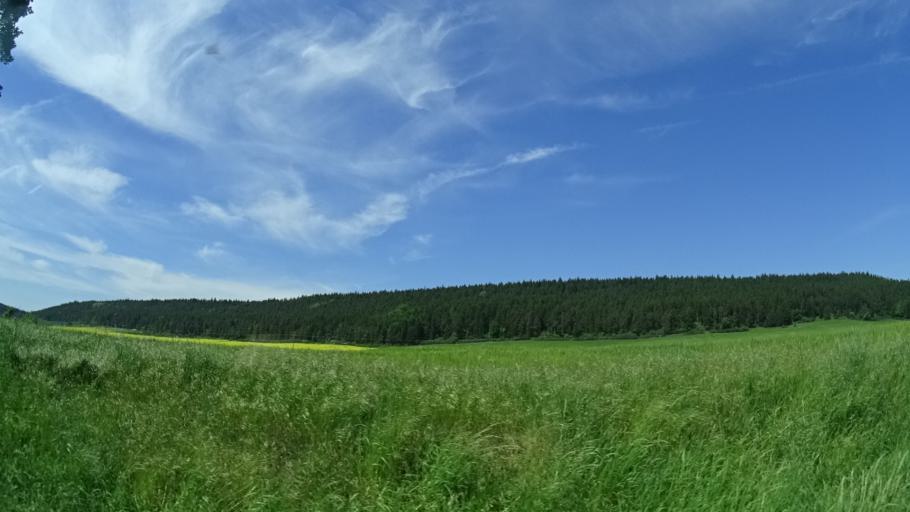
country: DE
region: Thuringia
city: Plaue
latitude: 50.7408
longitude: 10.9397
